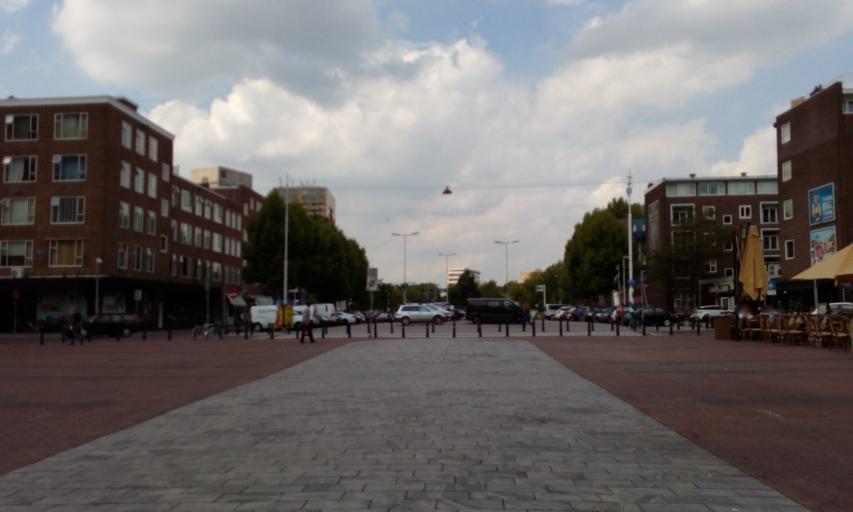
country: NL
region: South Holland
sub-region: Gemeente Rotterdam
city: Rotterdam
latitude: 51.9229
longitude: 4.4851
